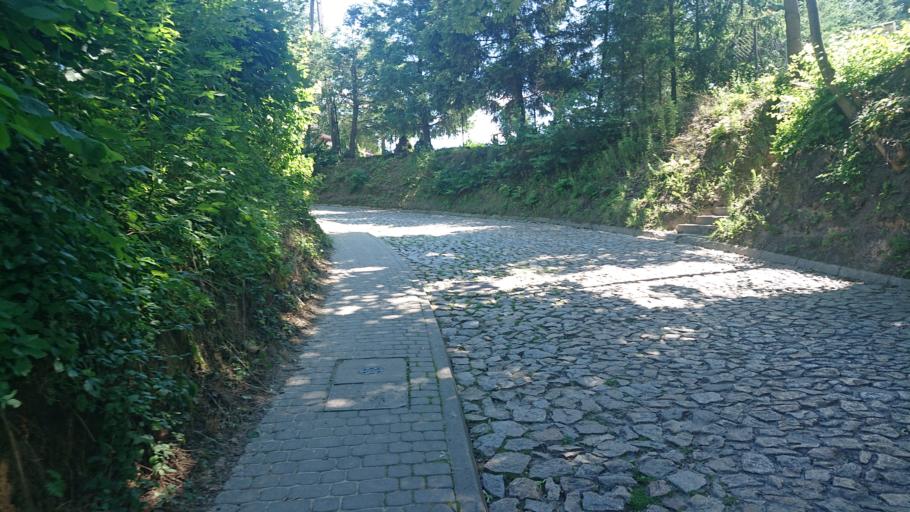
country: PL
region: Lublin Voivodeship
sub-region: Powiat pulawski
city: Kazimierz Dolny
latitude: 51.3237
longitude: 21.9550
